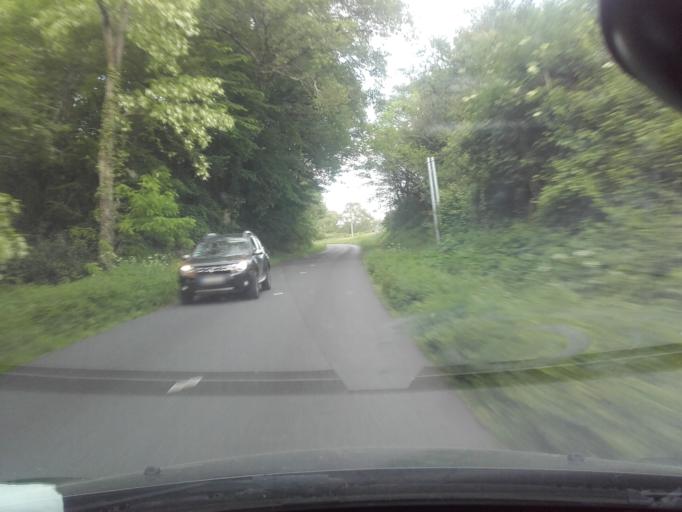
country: FR
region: Centre
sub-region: Departement du Loir-et-Cher
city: Chouzy-sur-Cisse
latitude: 47.5424
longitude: 1.2364
